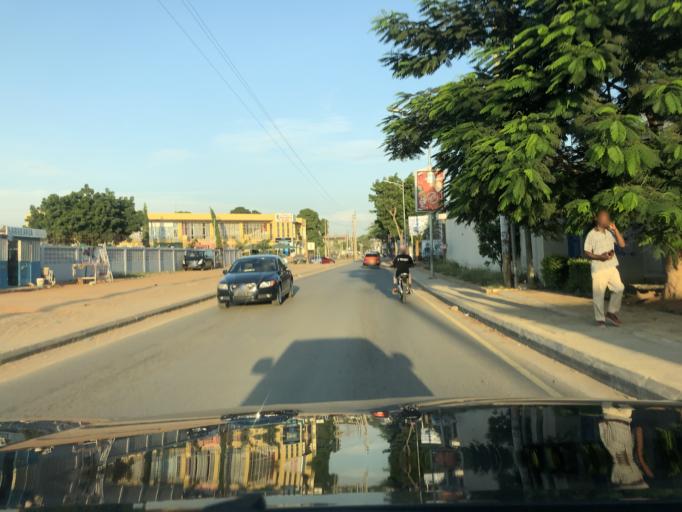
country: AO
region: Luanda
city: Luanda
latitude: -8.9486
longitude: 13.1678
